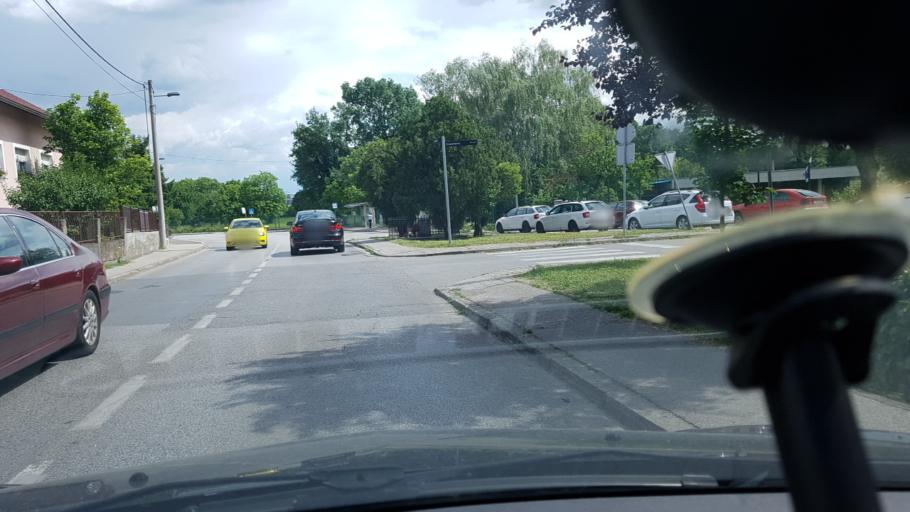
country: HR
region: Grad Zagreb
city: Dubrava
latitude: 45.8072
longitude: 16.0458
